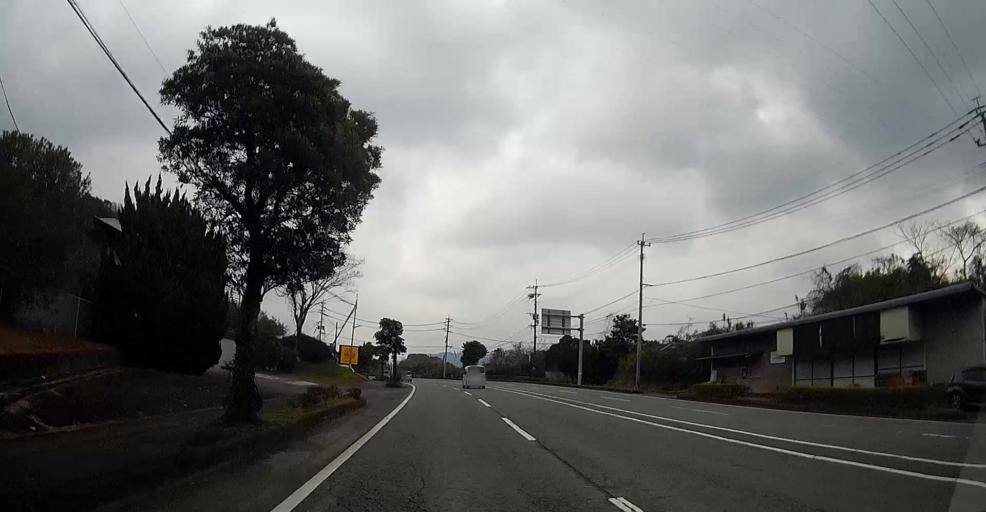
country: JP
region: Kumamoto
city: Matsubase
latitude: 32.6512
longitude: 130.7029
